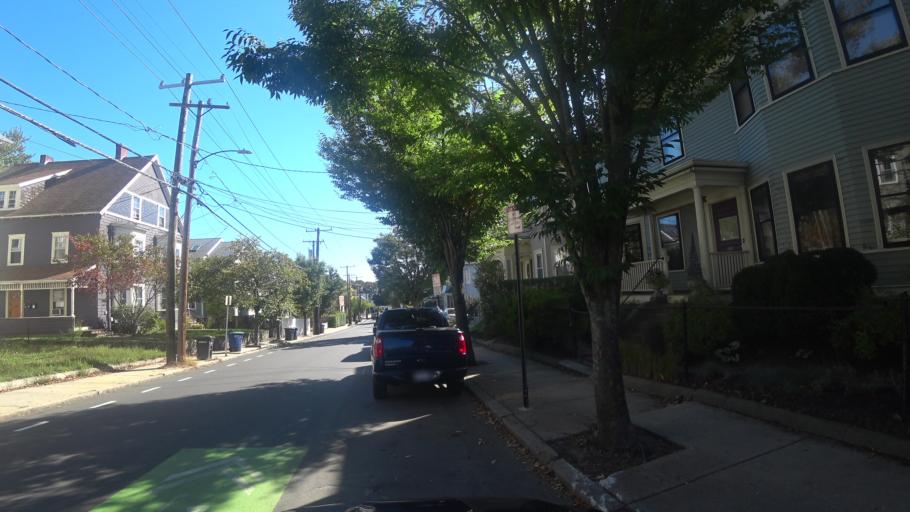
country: US
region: Massachusetts
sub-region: Middlesex County
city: Somerville
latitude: 42.3851
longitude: -71.1025
